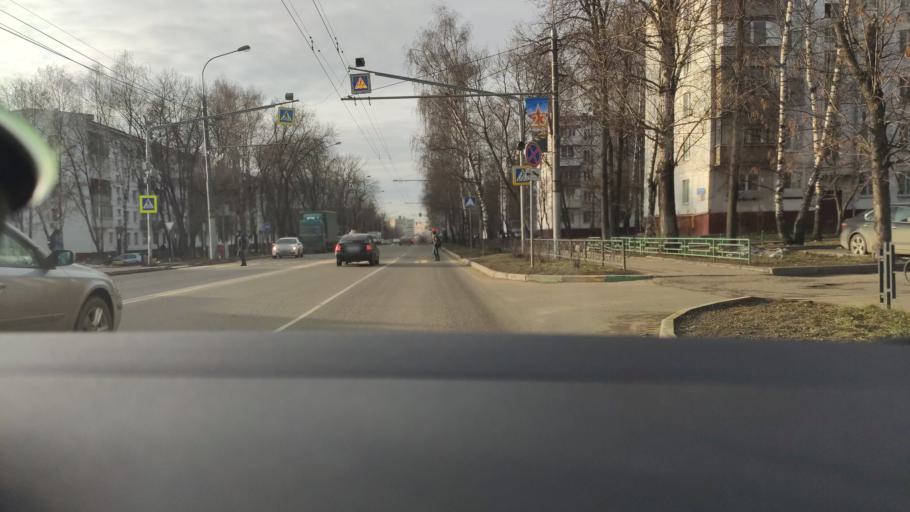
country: RU
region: Moskovskaya
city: Vidnoye
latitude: 55.5503
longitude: 37.7113
